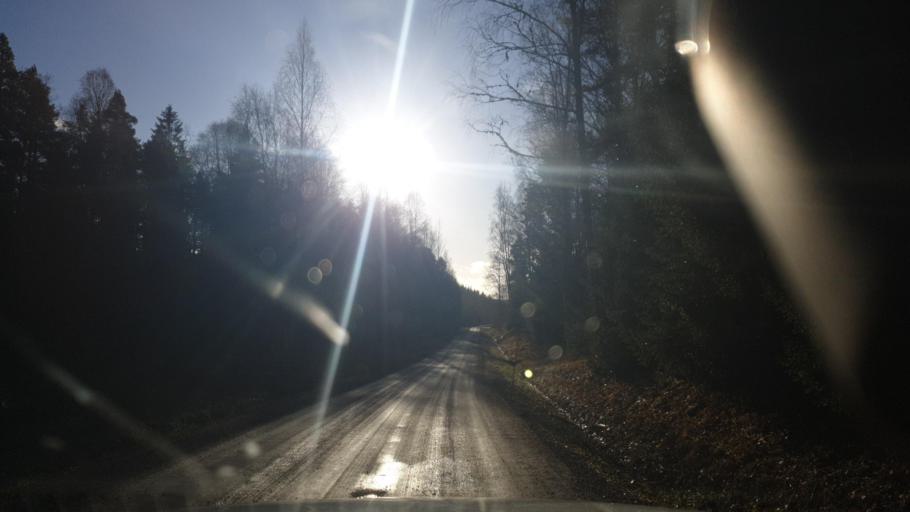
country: NO
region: Hedmark
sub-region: Eidskog
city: Skotterud
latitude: 59.8536
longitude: 11.9857
